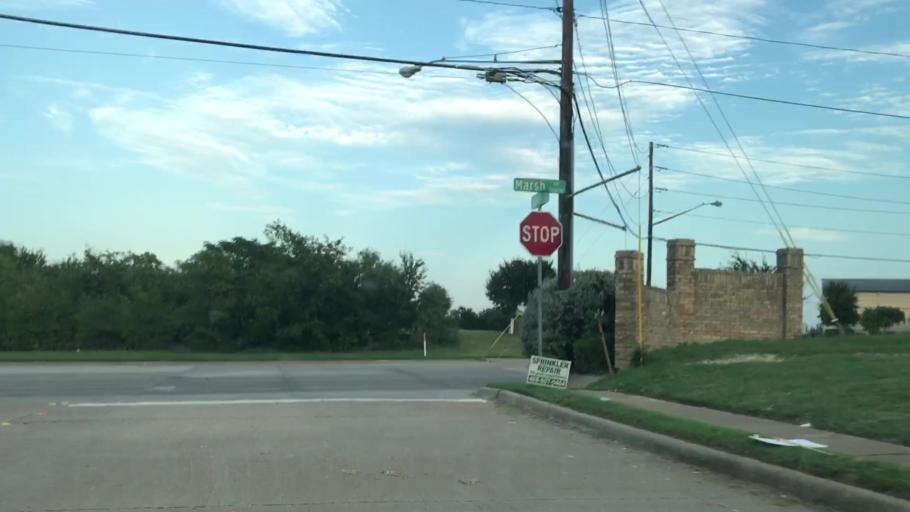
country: US
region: Texas
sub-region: Dallas County
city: Addison
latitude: 33.0045
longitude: -96.8576
